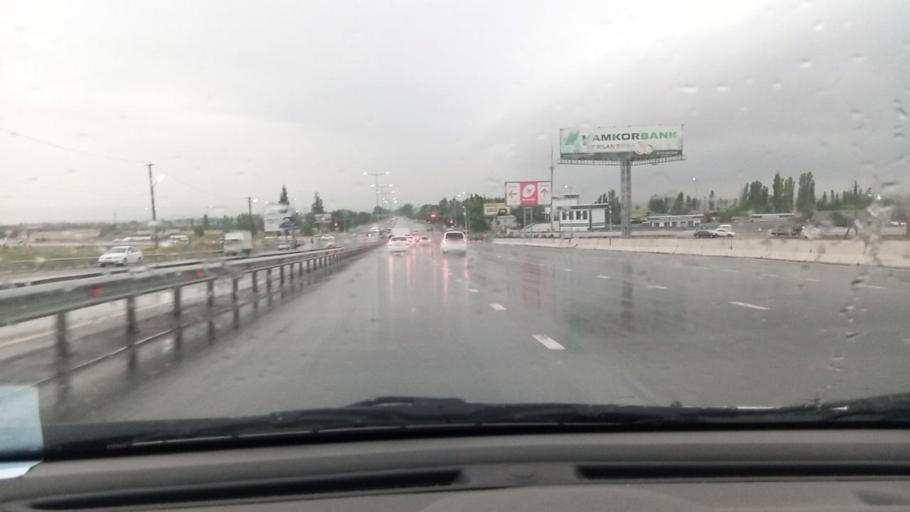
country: UZ
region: Toshkent
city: Ohangaron
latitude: 40.9224
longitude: 69.5970
